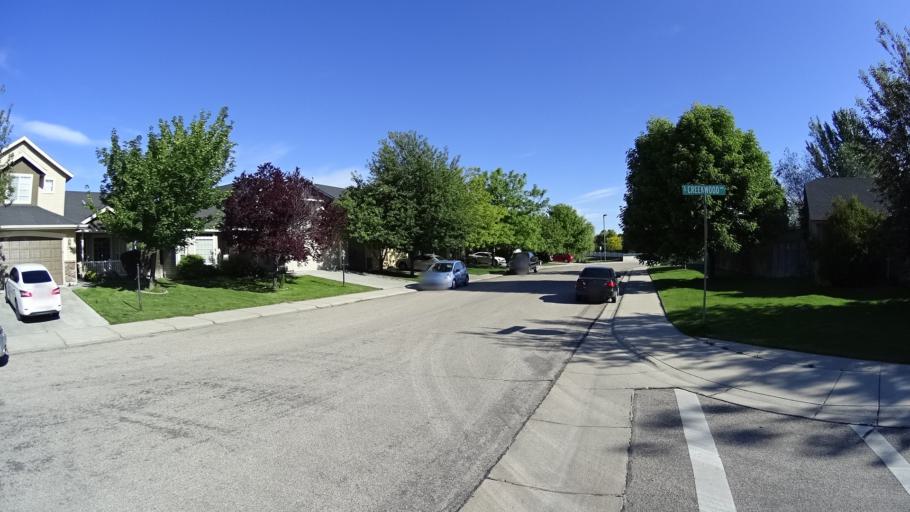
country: US
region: Idaho
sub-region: Ada County
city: Garden City
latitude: 43.5703
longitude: -116.2786
